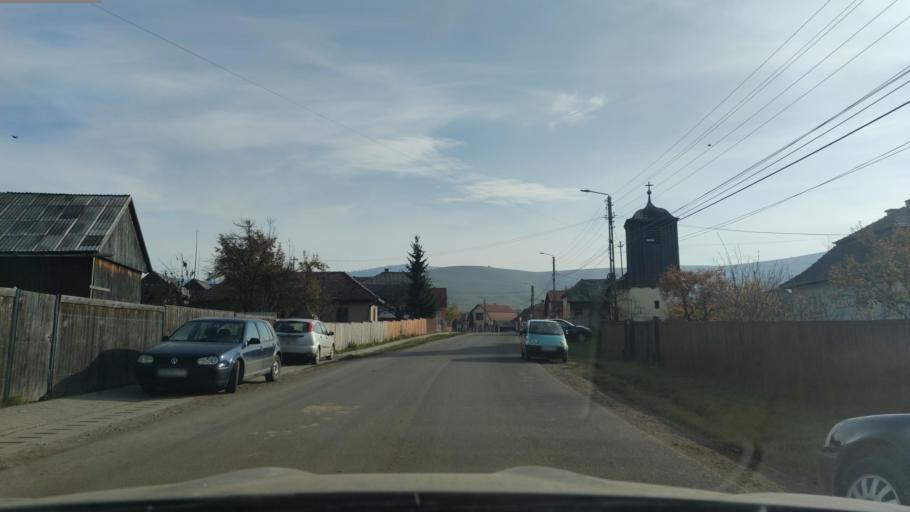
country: RO
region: Harghita
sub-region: Comuna Ditrau
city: Ditrau
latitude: 46.8091
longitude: 25.5102
